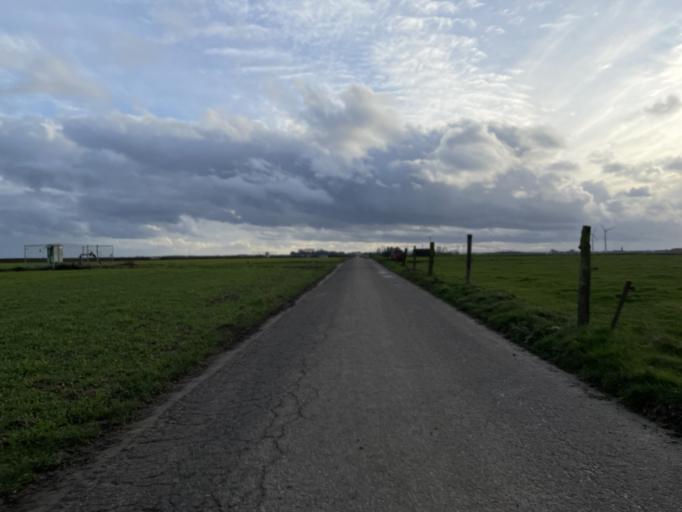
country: DE
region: North Rhine-Westphalia
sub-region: Regierungsbezirk Koln
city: Titz
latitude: 51.0804
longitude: 6.4172
